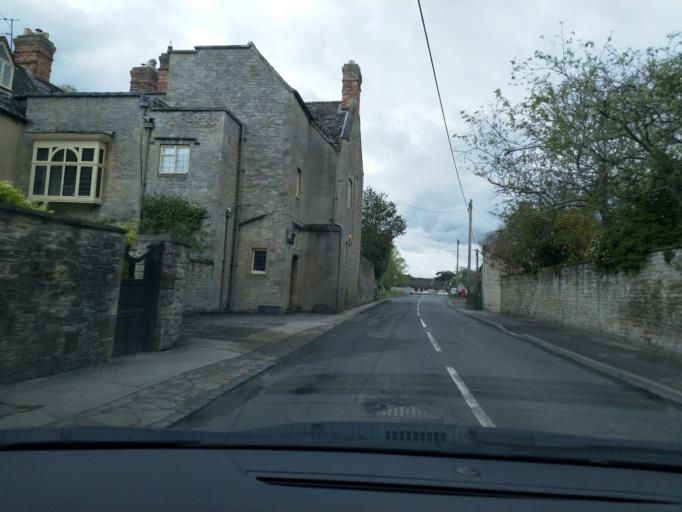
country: GB
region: England
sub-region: Oxfordshire
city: Eynsham
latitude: 51.7946
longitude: -1.3426
